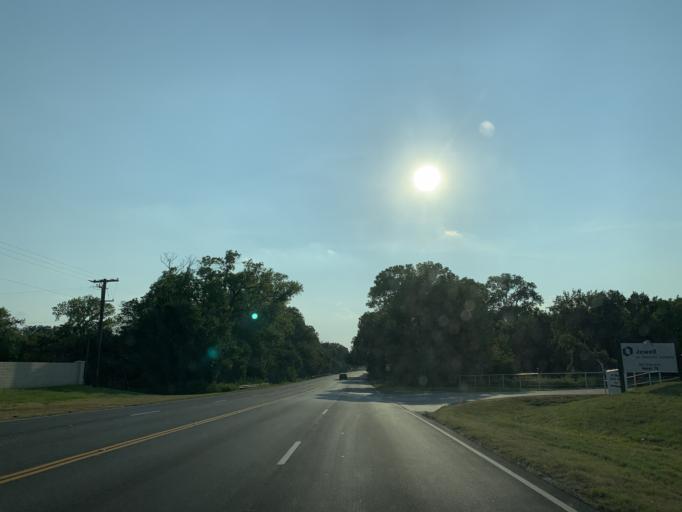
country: US
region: Texas
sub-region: Tarrant County
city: Hurst
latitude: 32.8021
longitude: -97.1758
